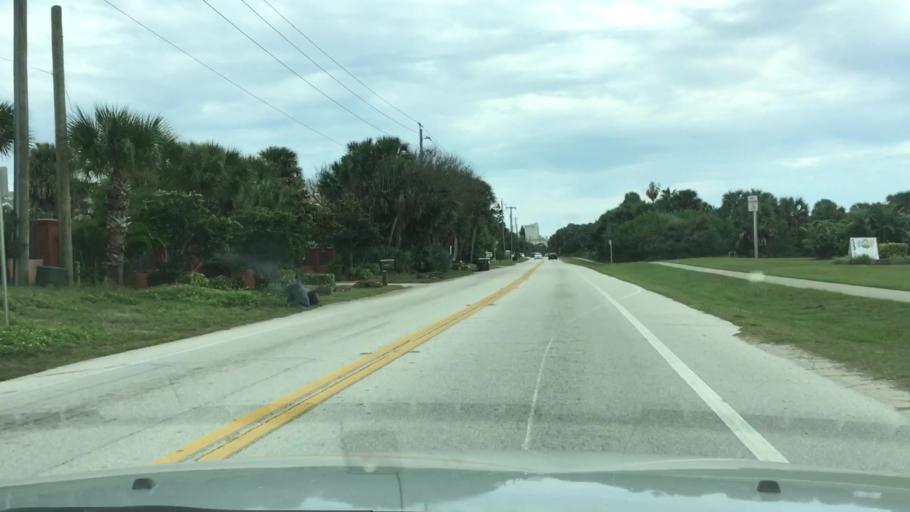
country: US
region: Florida
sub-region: Volusia County
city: Ormond Beach
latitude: 29.3010
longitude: -81.0445
